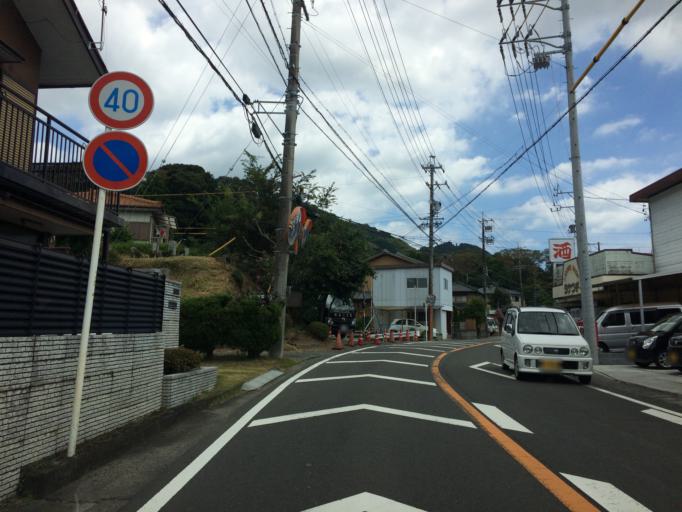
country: JP
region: Shizuoka
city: Yaizu
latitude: 34.9038
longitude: 138.2938
